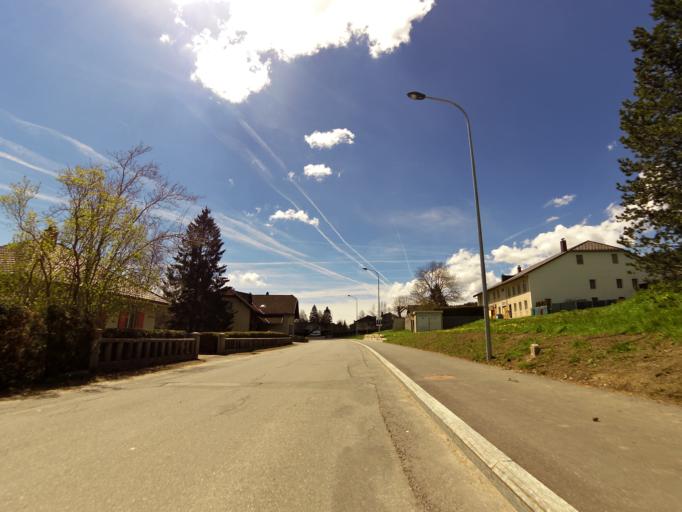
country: CH
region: Vaud
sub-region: Jura-Nord vaudois District
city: Le Chenit
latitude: 46.5949
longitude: 6.2151
